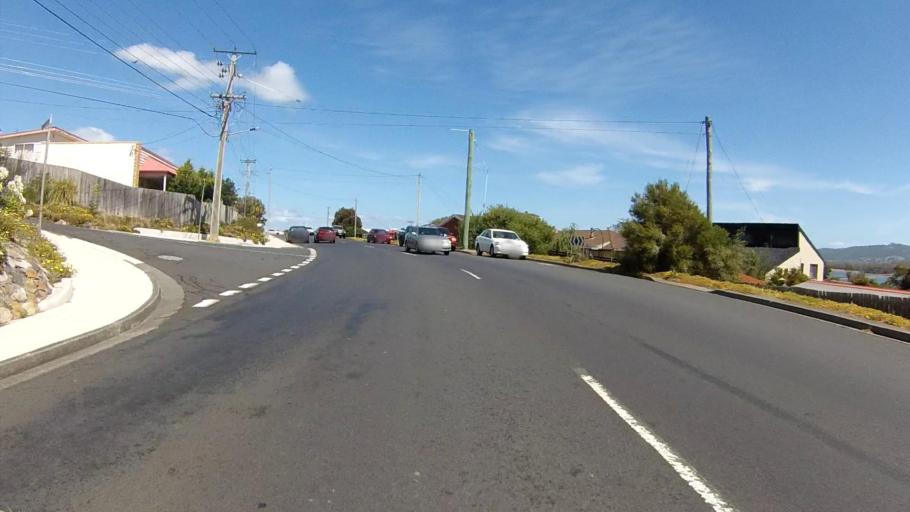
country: AU
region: Tasmania
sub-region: Sorell
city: Sorell
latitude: -42.7994
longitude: 147.5284
